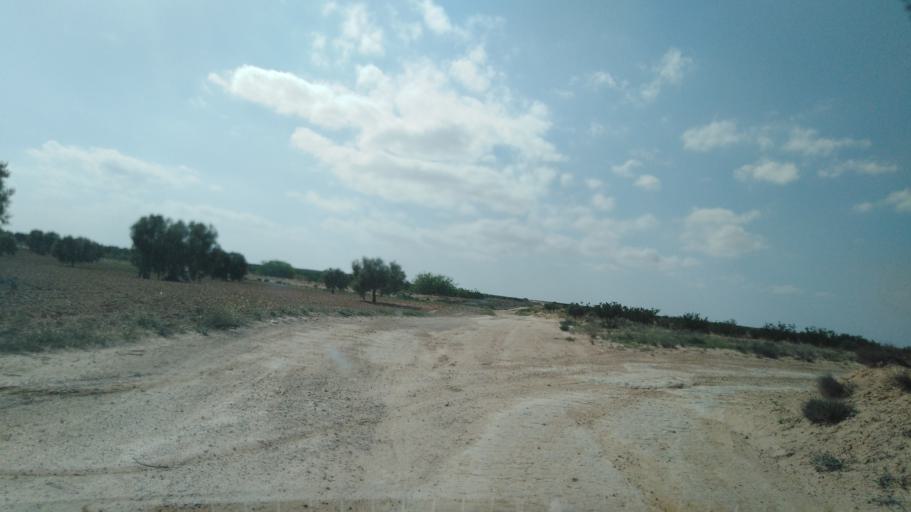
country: TN
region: Safaqis
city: Bi'r `Ali Bin Khalifah
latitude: 34.8004
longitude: 10.3804
